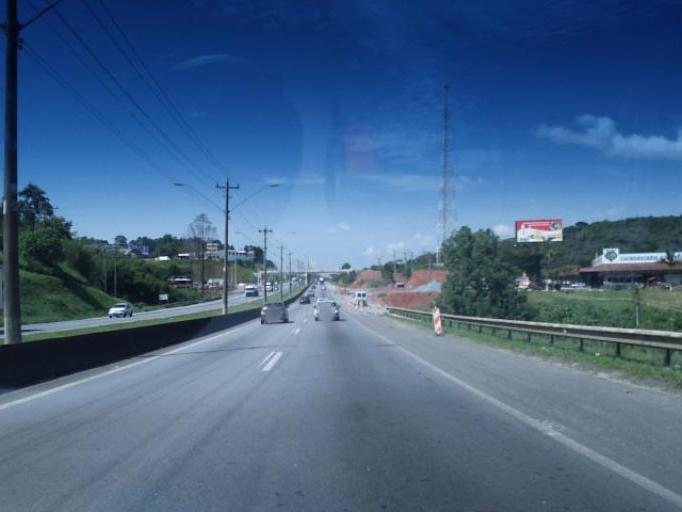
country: BR
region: Sao Paulo
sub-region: Itapecerica Da Serra
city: Itapecerica da Serra
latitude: -23.7047
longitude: -46.8732
